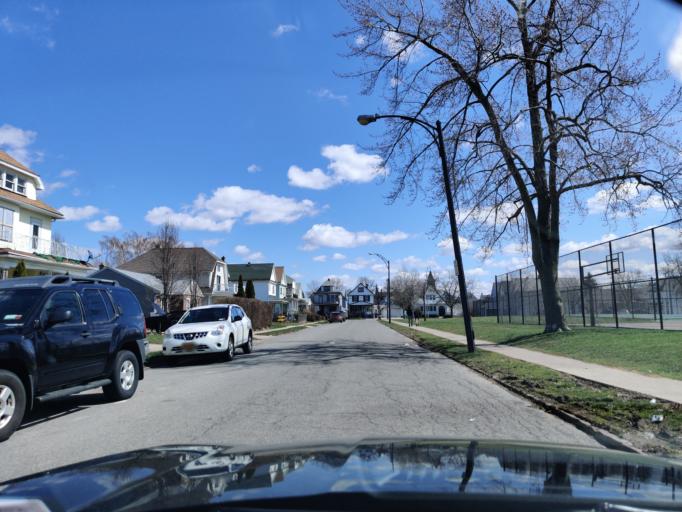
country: US
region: New York
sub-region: Erie County
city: Sloan
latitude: 42.8880
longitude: -78.8112
